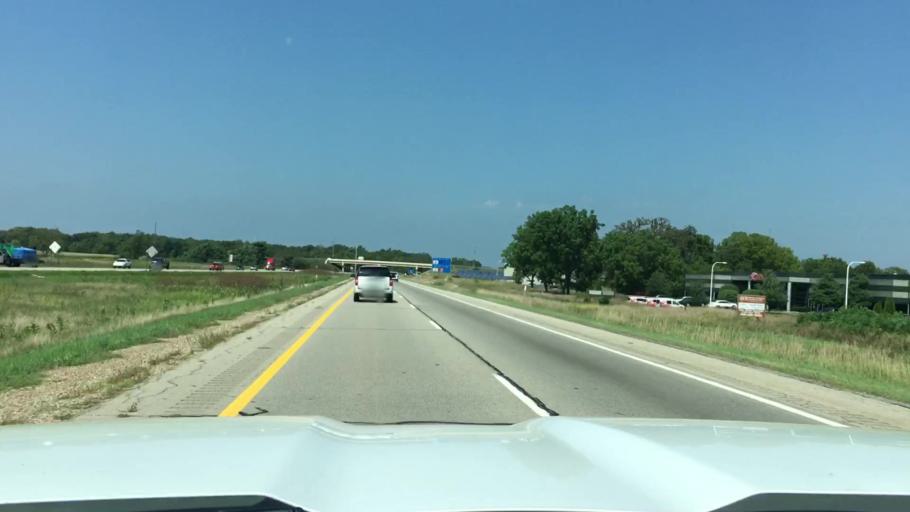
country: US
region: Michigan
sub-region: Kalamazoo County
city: Westwood
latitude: 42.2560
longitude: -85.6477
